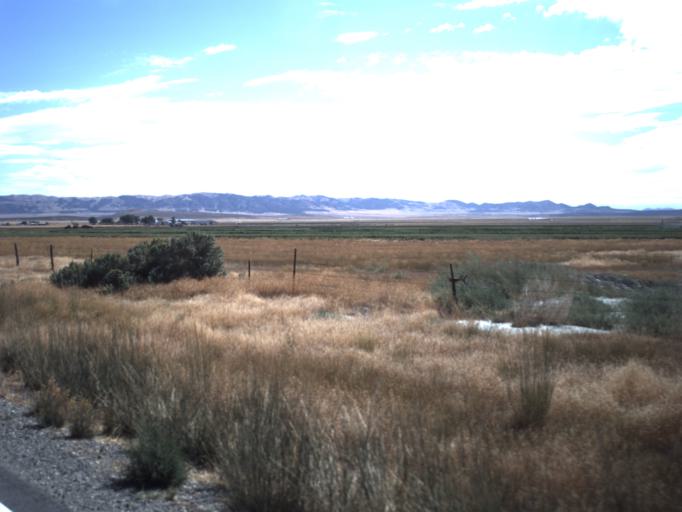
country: US
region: Idaho
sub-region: Oneida County
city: Malad City
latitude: 41.9671
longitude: -112.8623
